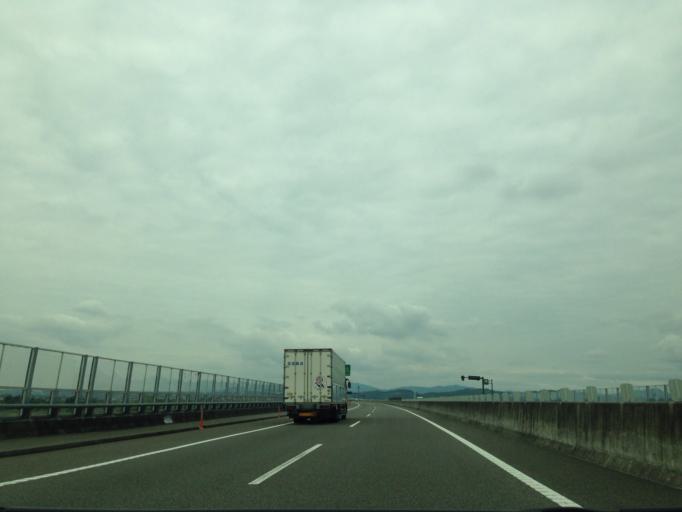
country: JP
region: Shizuoka
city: Hamakita
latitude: 34.8318
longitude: 137.8346
